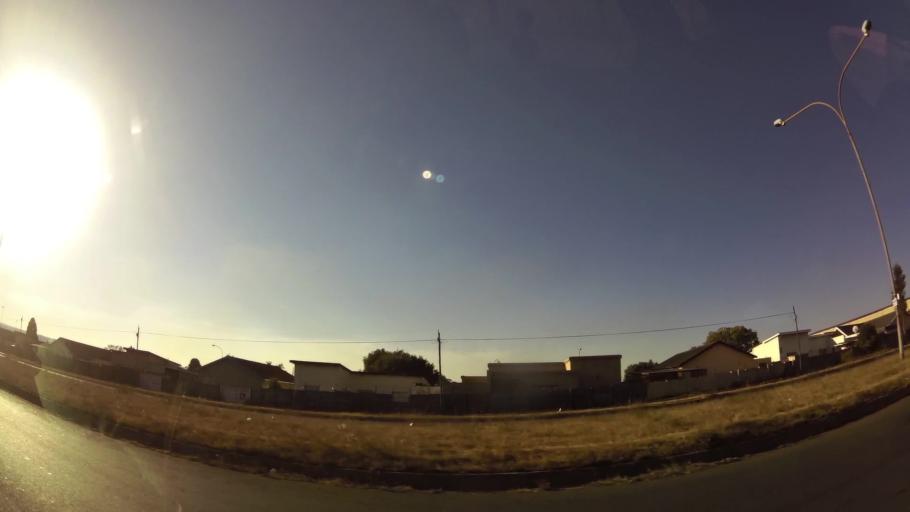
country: ZA
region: Gauteng
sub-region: City of Johannesburg Metropolitan Municipality
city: Johannesburg
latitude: -26.2065
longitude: 27.9600
